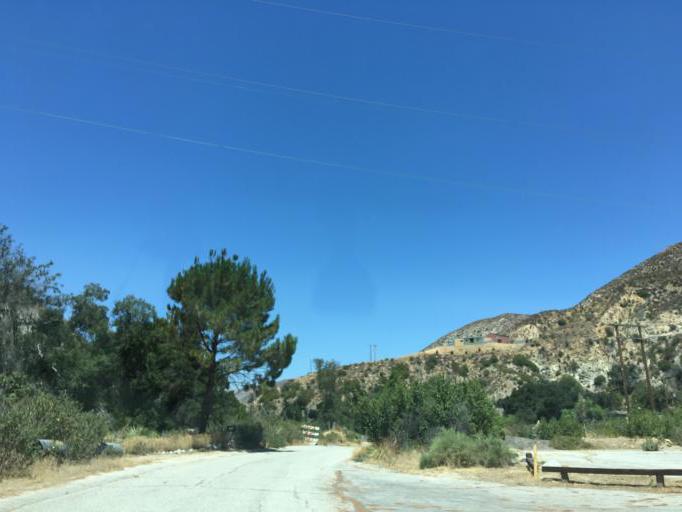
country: US
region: California
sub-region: Los Angeles County
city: La Crescenta-Montrose
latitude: 34.2869
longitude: -118.2282
